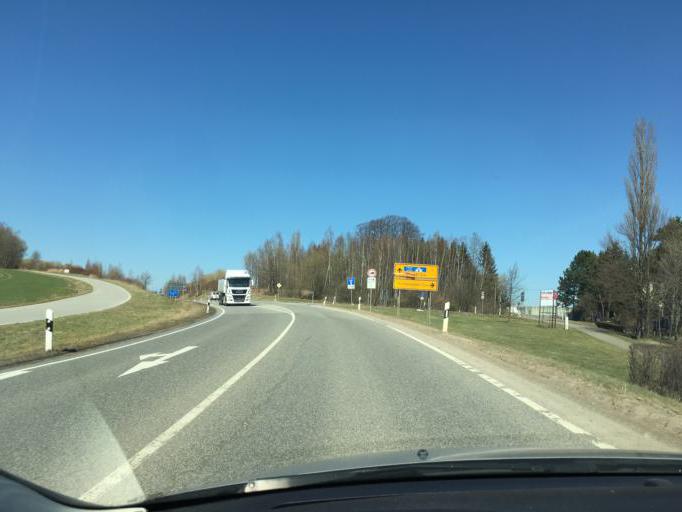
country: DE
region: Saxony
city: Limbach-Oberfrohna
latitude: 50.8763
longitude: 12.7819
